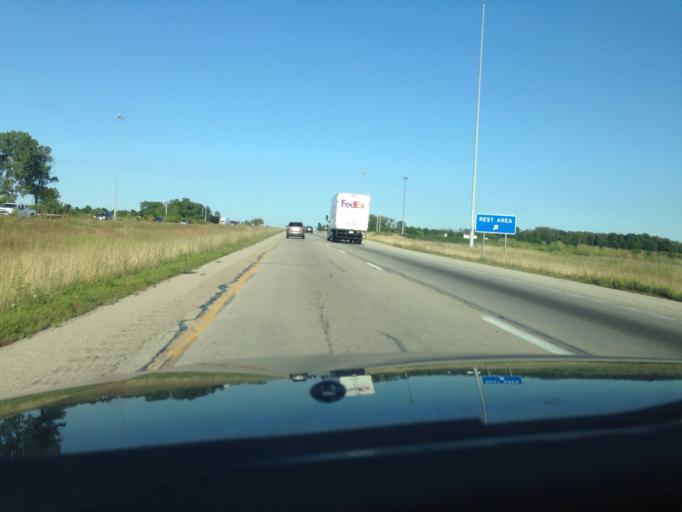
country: US
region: Ohio
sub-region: Preble County
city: New Paris
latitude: 39.8285
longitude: -84.7695
